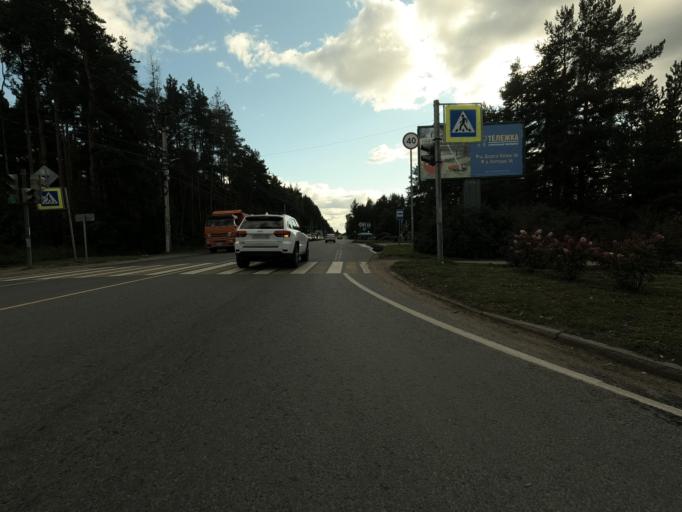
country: RU
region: Leningrad
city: Vsevolozhsk
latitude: 59.9953
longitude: 30.6597
